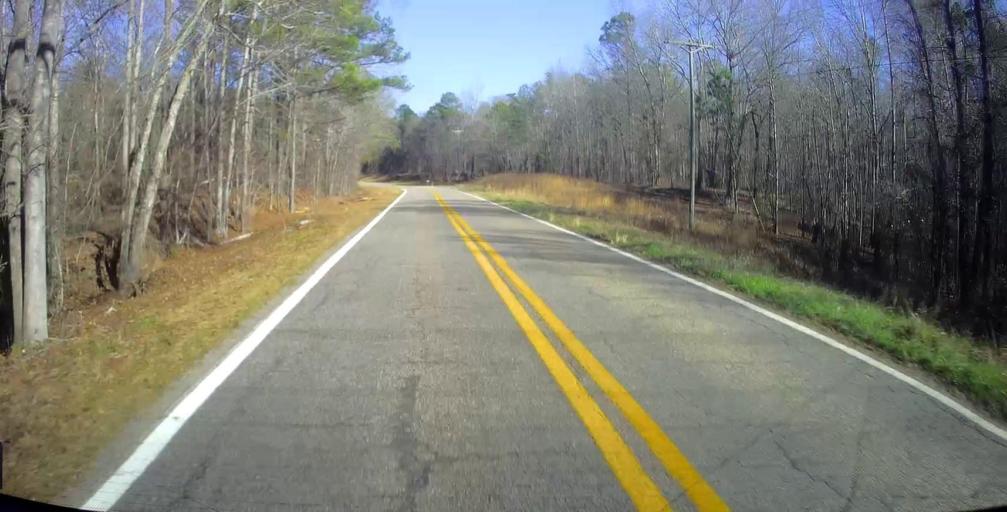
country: US
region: Georgia
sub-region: Peach County
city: Fort Valley
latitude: 32.6466
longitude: -83.8958
